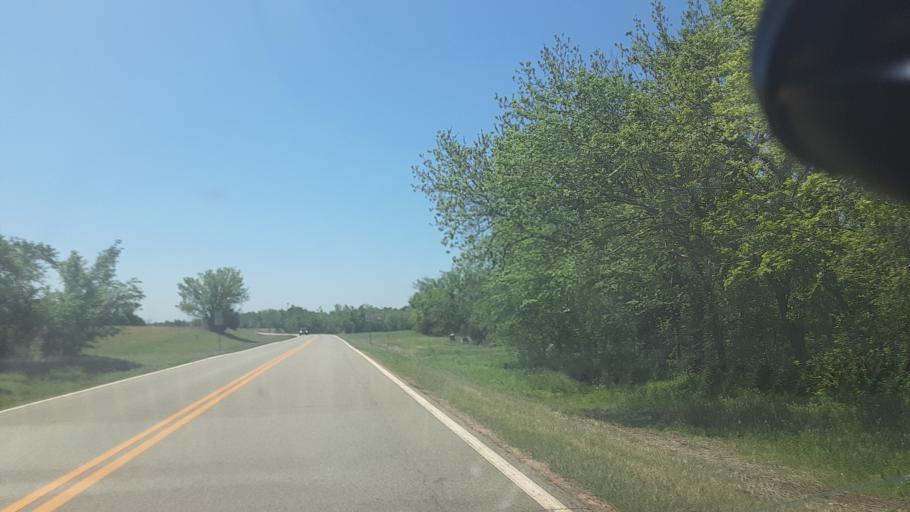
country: US
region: Oklahoma
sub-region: Noble County
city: Perry
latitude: 36.1080
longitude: -97.3908
